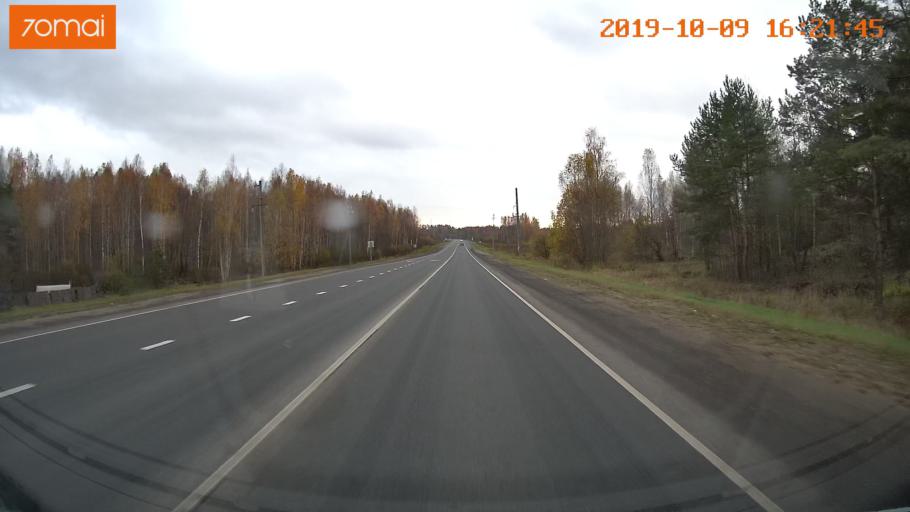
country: RU
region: Kostroma
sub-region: Kostromskoy Rayon
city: Kostroma
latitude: 57.6871
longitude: 40.8881
